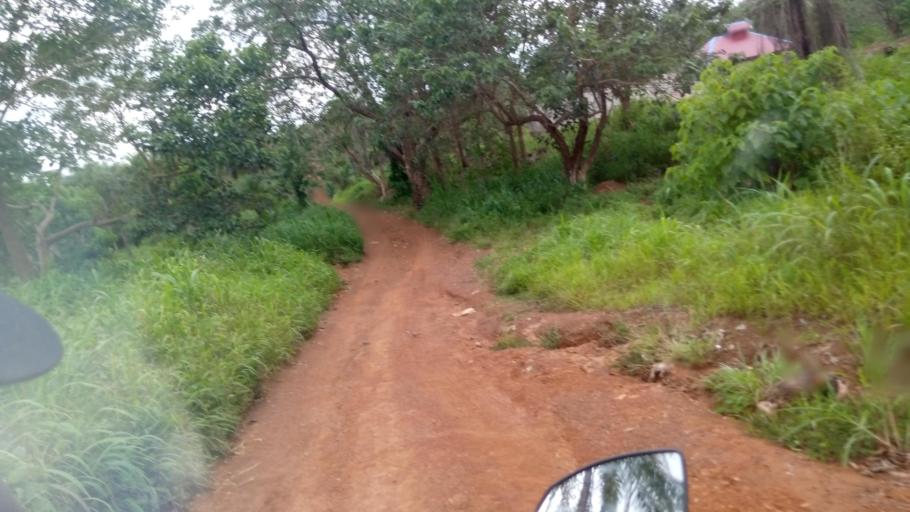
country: SL
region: Northern Province
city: Kamakwie
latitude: 9.4940
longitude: -12.2331
